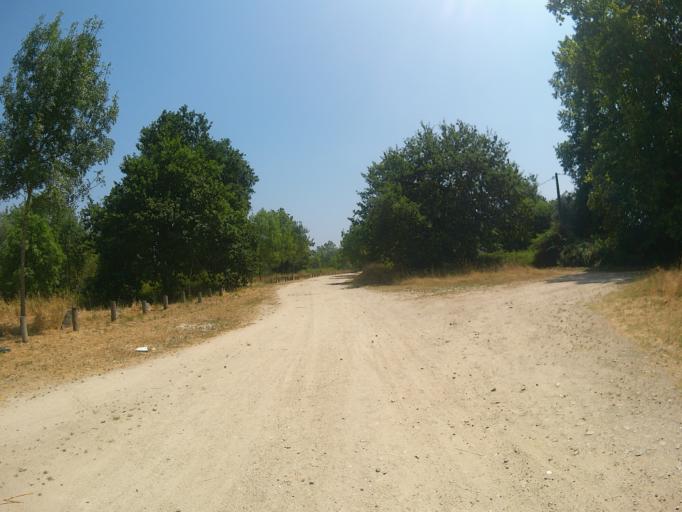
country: PT
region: Viana do Castelo
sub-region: Ponte de Lima
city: Ponte de Lima
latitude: 41.7769
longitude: -8.5768
